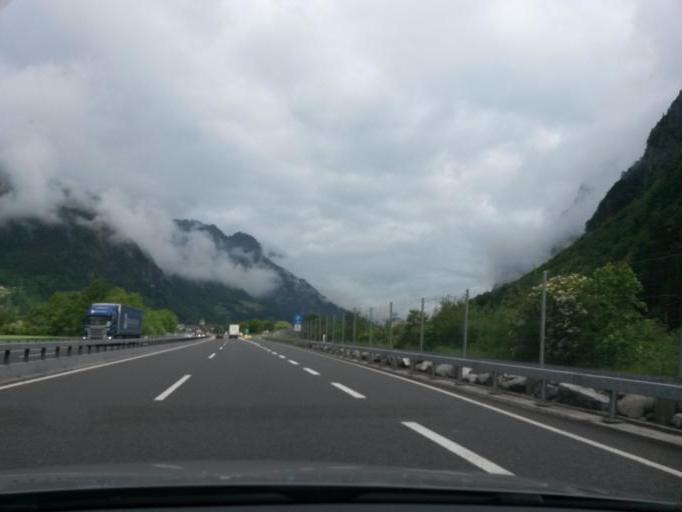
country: CH
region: Uri
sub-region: Uri
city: Erstfeld
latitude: 46.8115
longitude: 8.6578
